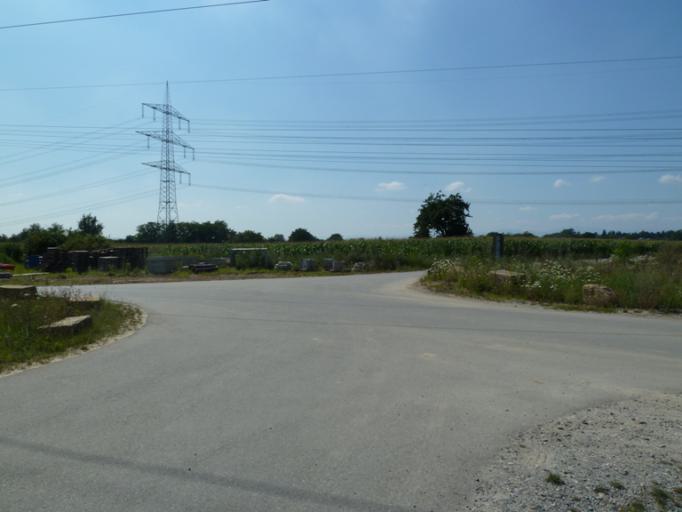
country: DE
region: Baden-Wuerttemberg
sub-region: Freiburg Region
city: Schliengen
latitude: 47.7608
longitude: 7.5681
